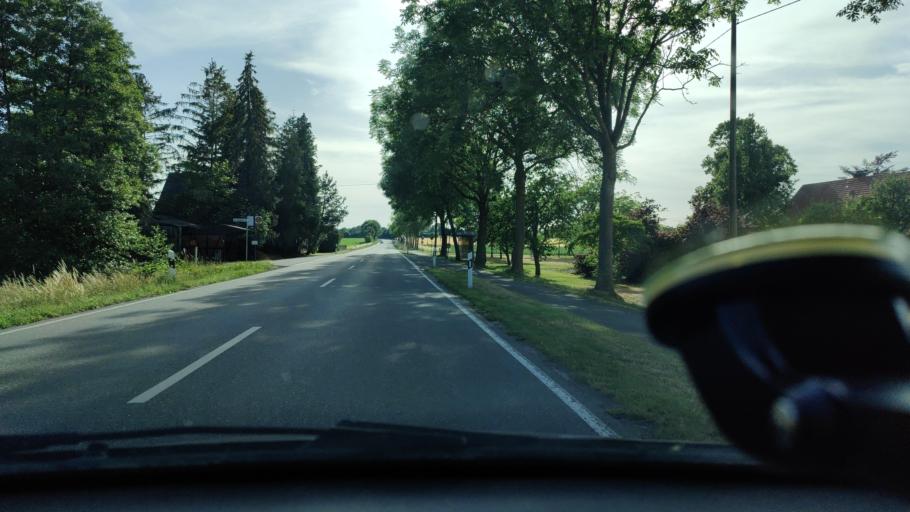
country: DE
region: North Rhine-Westphalia
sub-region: Regierungsbezirk Munster
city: Billerbeck
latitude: 52.0236
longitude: 7.2451
